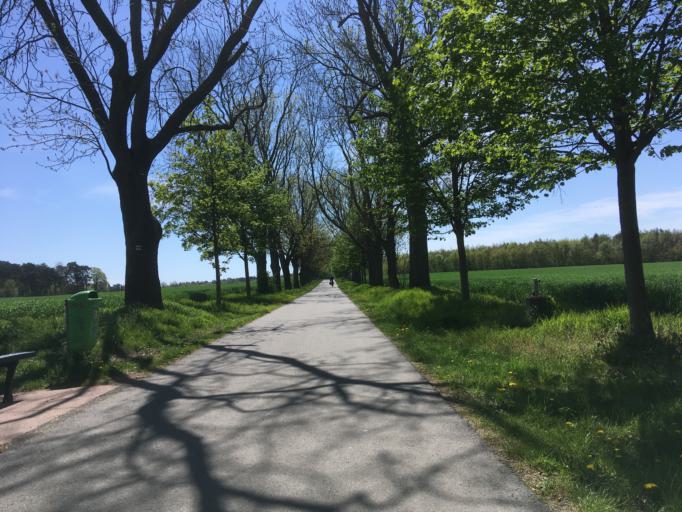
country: DE
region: Brandenburg
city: Wildau
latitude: 52.3176
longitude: 13.6138
